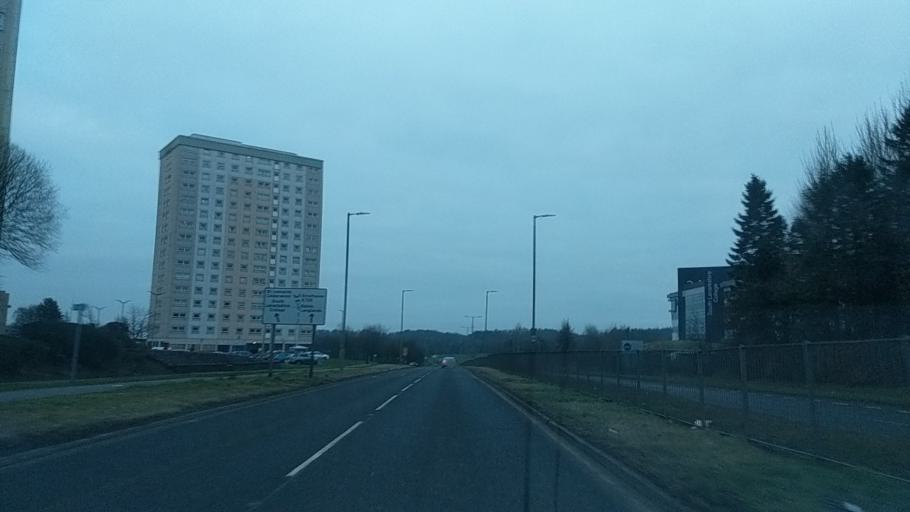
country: GB
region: Scotland
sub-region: South Lanarkshire
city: East Kilbride
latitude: 55.7552
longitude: -4.1597
